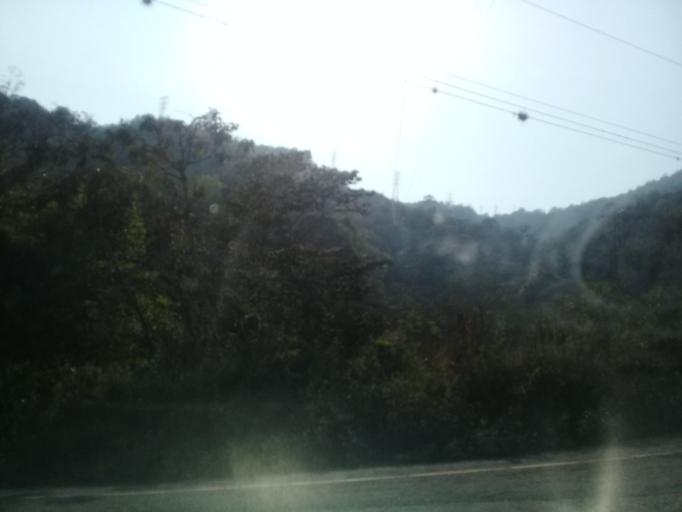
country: MX
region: Veracruz
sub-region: Ixtaczoquitlan
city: Campo Chico
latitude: 18.8365
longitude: -97.0364
